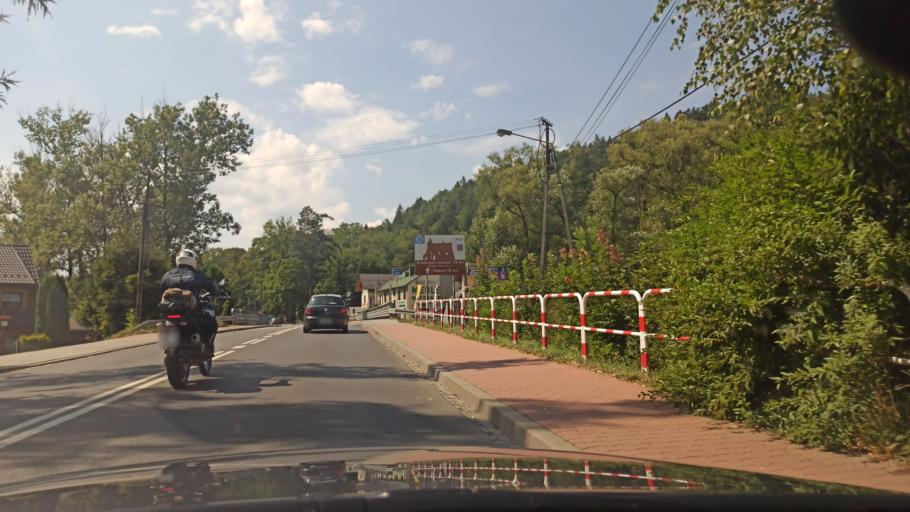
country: PL
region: Lesser Poland Voivodeship
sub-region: Powiat nowotarski
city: Kroscienko nad Dunajcem
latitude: 49.4407
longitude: 20.4183
